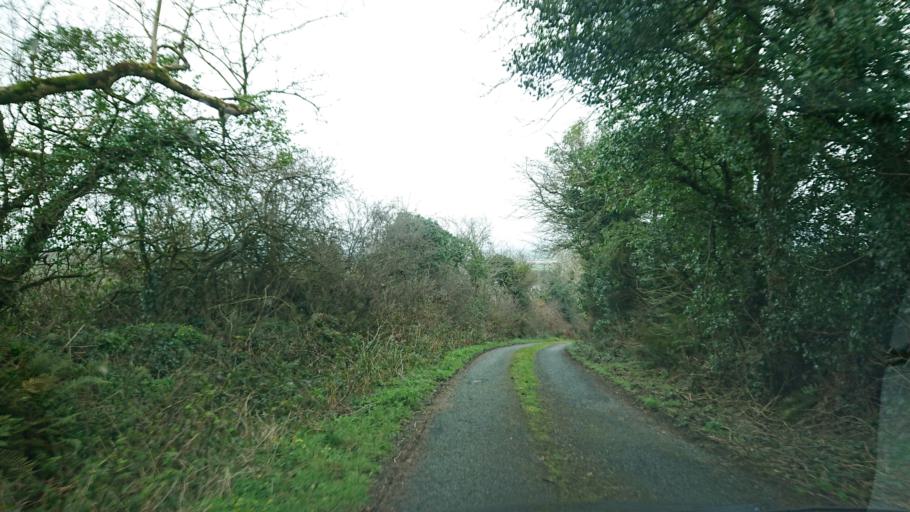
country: IE
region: Munster
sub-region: Waterford
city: Waterford
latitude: 52.2662
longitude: -7.0071
